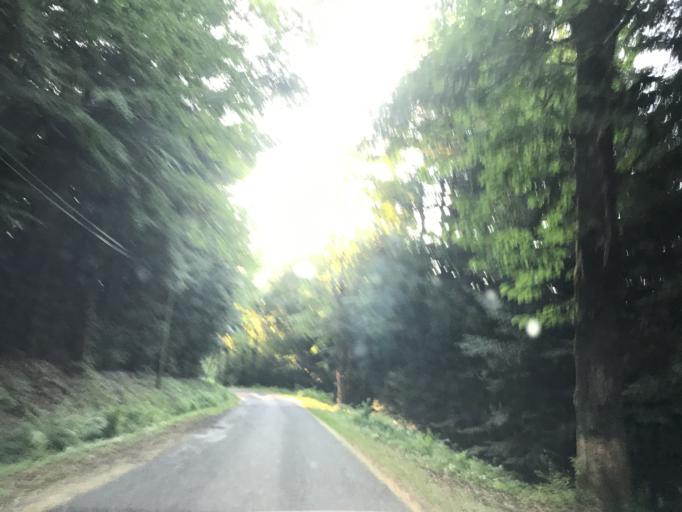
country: FR
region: Auvergne
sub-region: Departement du Puy-de-Dome
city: Courpiere
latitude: 45.7553
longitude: 3.6444
